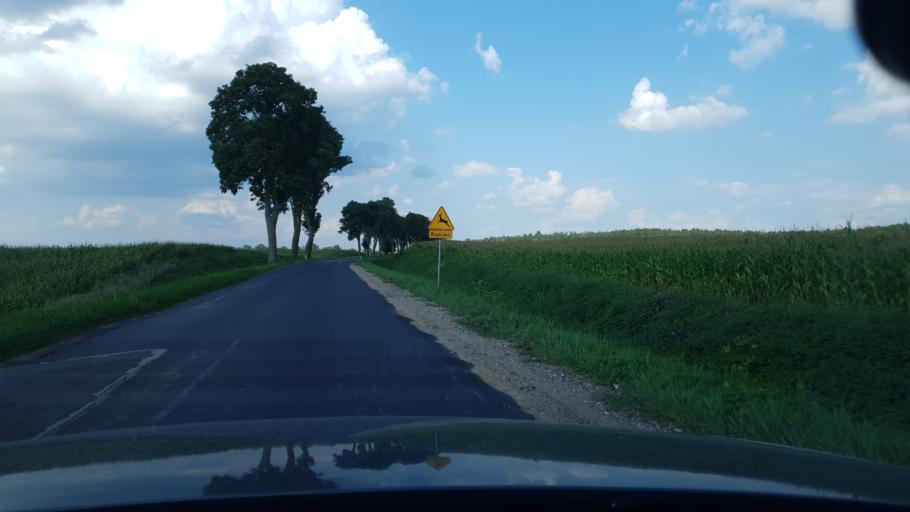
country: PL
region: Kujawsko-Pomorskie
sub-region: Powiat wabrzeski
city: Wabrzezno
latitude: 53.2559
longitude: 18.8869
